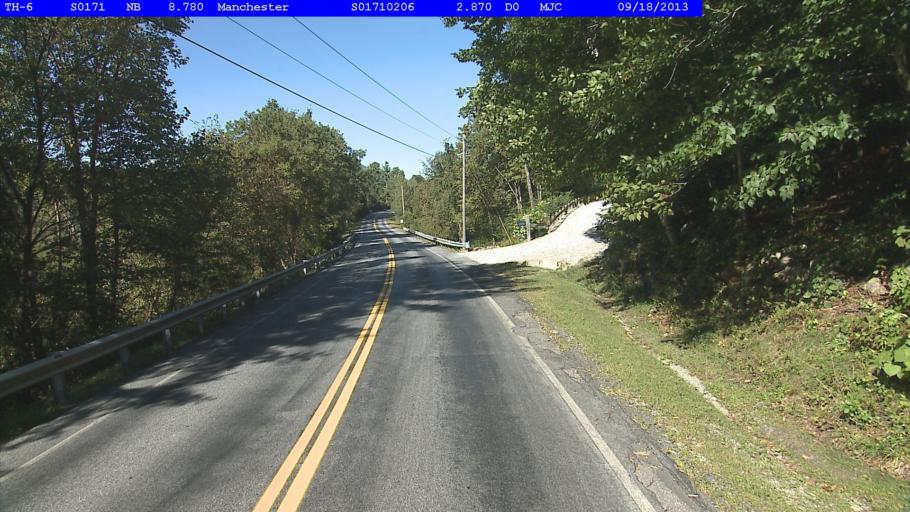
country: US
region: Vermont
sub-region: Bennington County
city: Manchester Center
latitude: 43.1462
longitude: -73.0545
